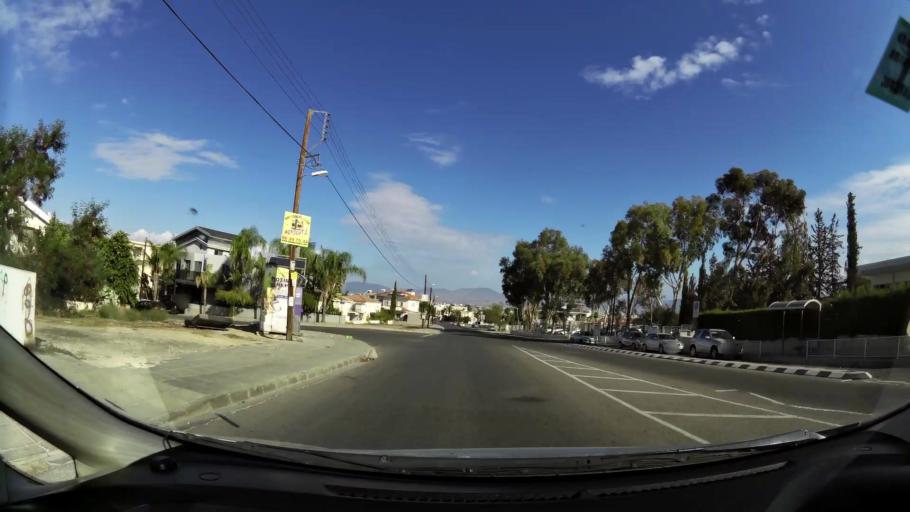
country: CY
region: Lefkosia
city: Nicosia
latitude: 35.1274
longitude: 33.3437
